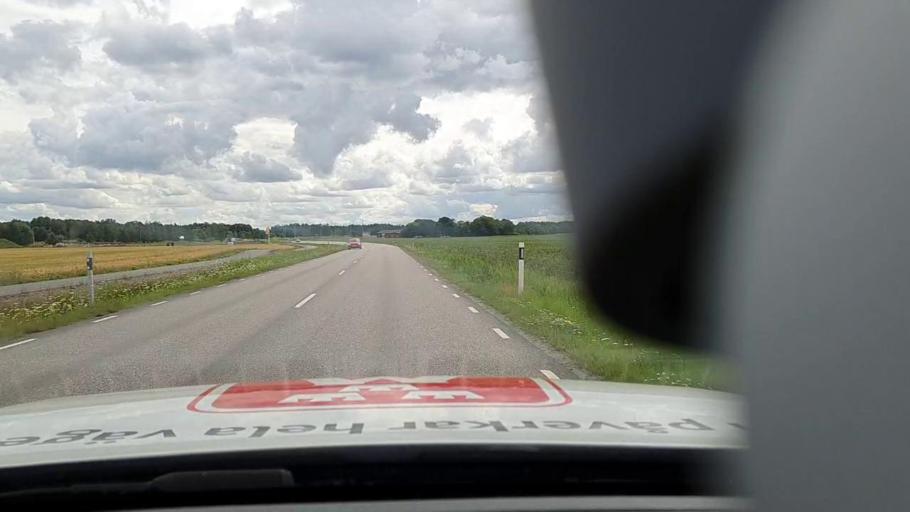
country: SE
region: Vaestra Goetaland
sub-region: Lidkopings Kommun
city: Lidkoping
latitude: 58.5467
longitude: 13.1138
